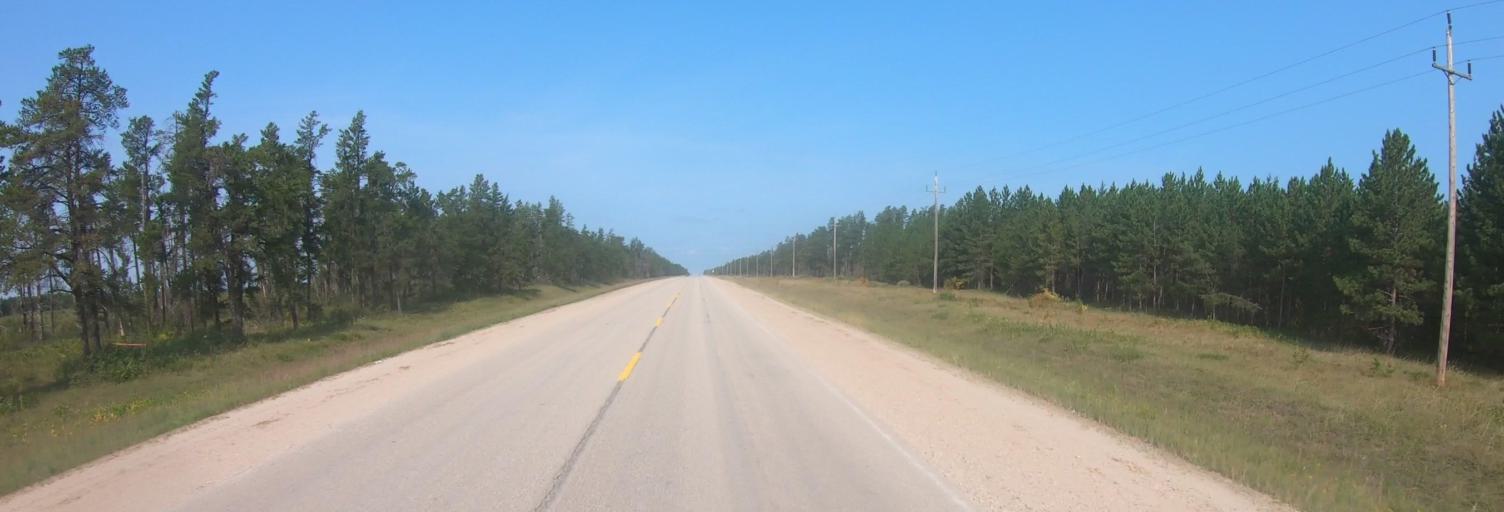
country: US
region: Minnesota
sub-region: Roseau County
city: Roseau
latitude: 49.1223
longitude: -96.0601
